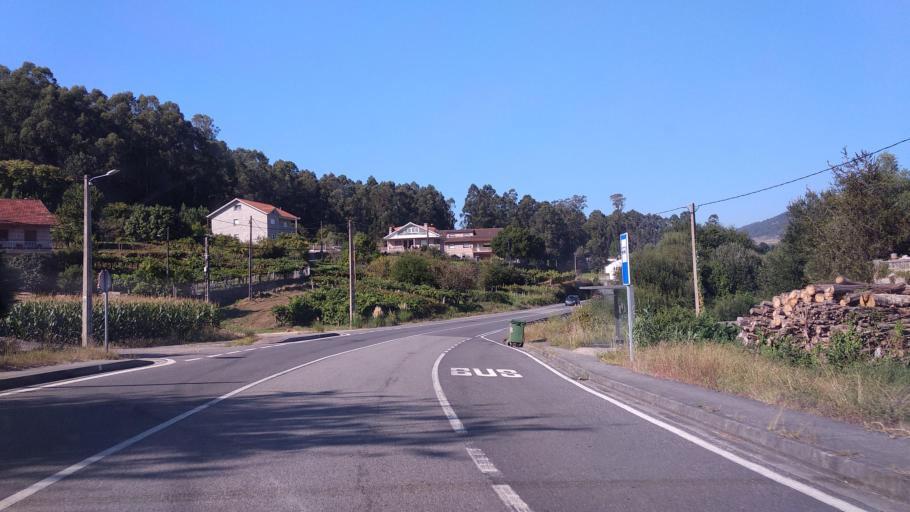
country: ES
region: Galicia
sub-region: Provincia de Pontevedra
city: Marin
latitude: 42.3515
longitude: -8.6418
